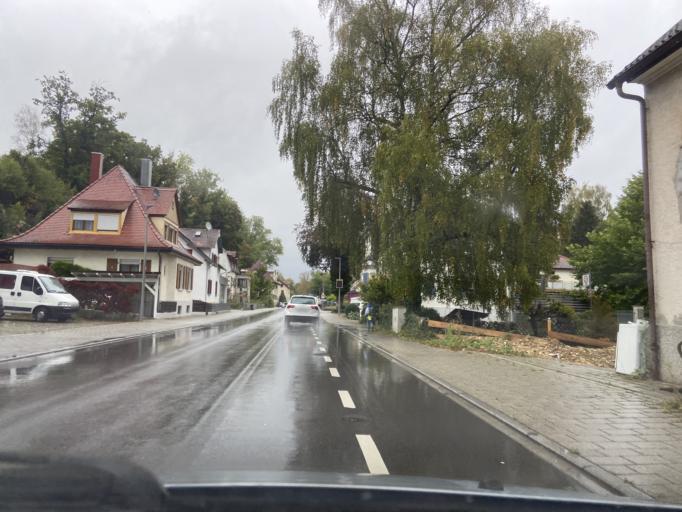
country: DE
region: Baden-Wuerttemberg
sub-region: Tuebingen Region
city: Sigmaringendorf
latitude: 48.0699
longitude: 9.2641
